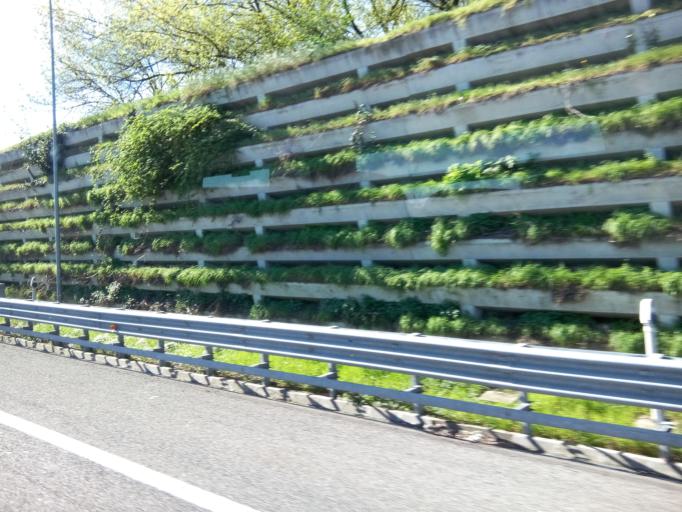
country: IT
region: Lombardy
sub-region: Citta metropolitana di Milano
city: Pero
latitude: 45.5318
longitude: 9.0901
